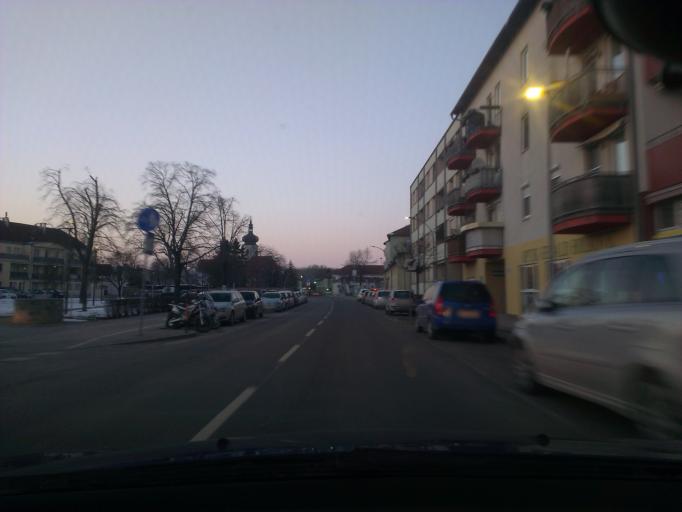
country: AT
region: Lower Austria
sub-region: Politischer Bezirk Wien-Umgebung
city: Fischamend Dorf
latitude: 48.1174
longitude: 16.6138
